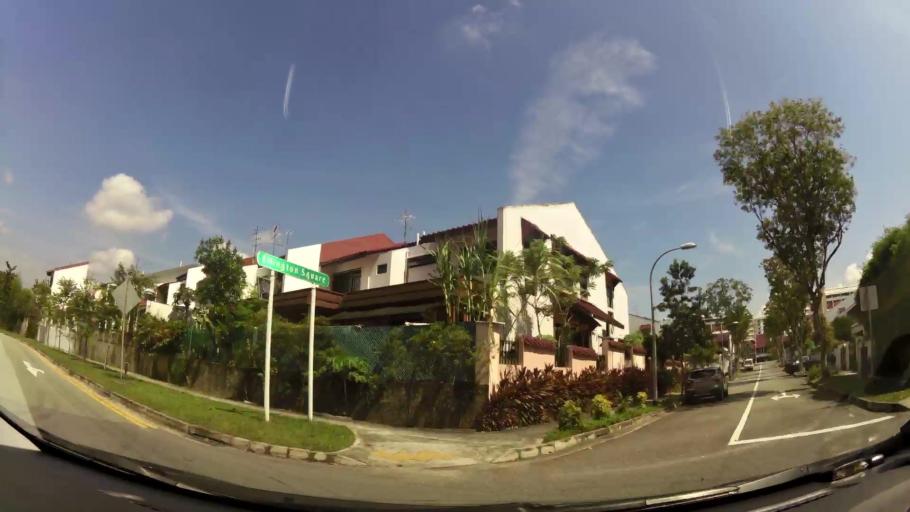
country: SG
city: Singapore
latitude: 1.3711
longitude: 103.8345
